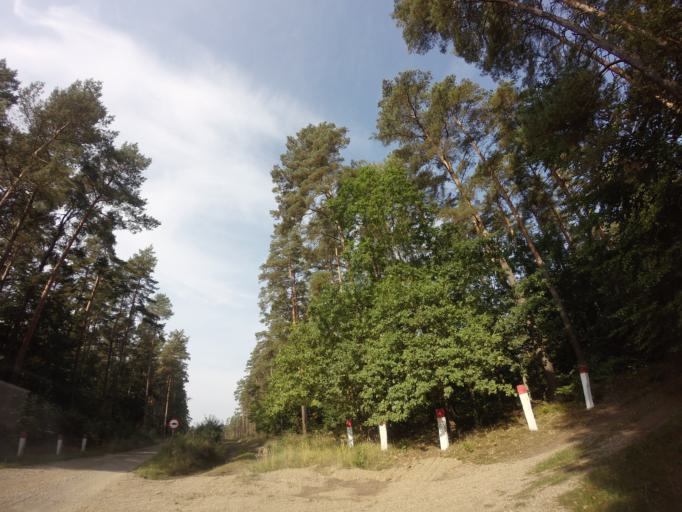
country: PL
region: West Pomeranian Voivodeship
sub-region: Powiat drawski
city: Drawsko Pomorskie
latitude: 53.4584
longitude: 15.7283
